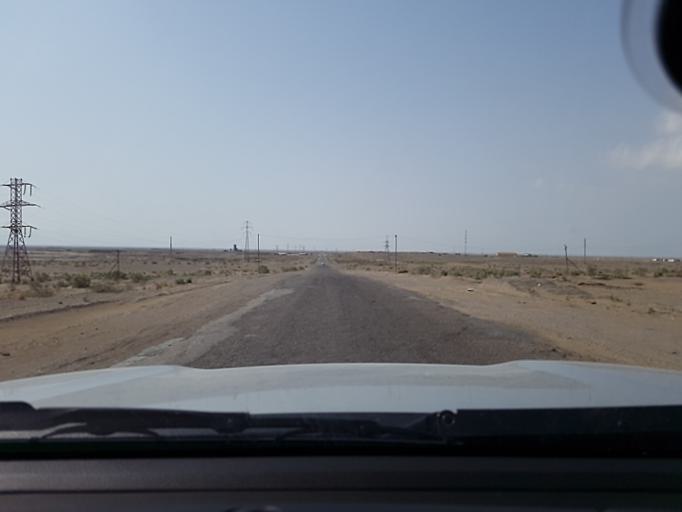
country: TM
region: Balkan
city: Gumdag
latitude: 39.1265
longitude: 54.5779
